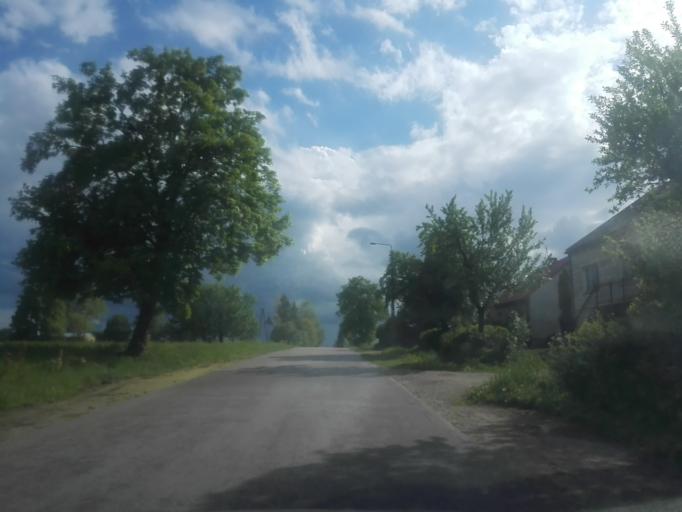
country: PL
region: Podlasie
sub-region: Powiat lomzynski
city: Wizna
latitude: 53.2284
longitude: 22.4217
